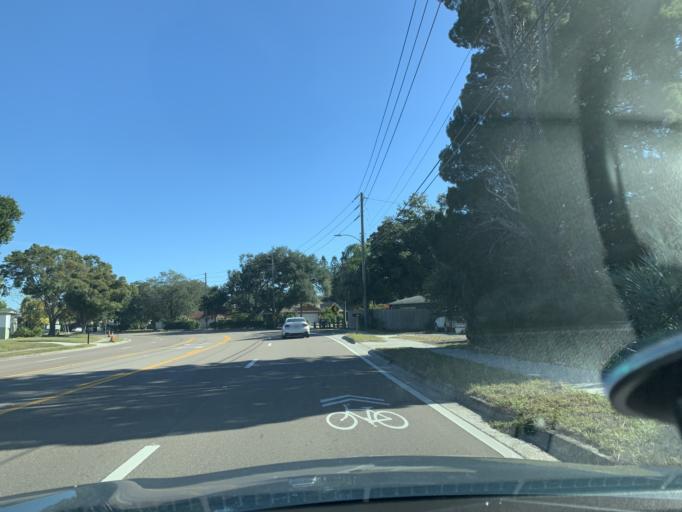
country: US
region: Florida
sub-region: Pinellas County
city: Gulfport
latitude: 27.7487
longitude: -82.7154
